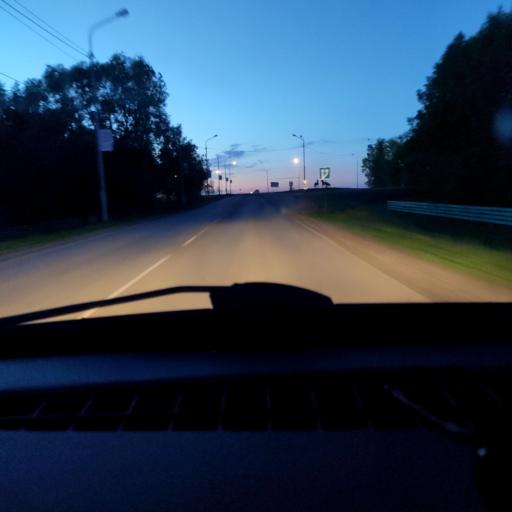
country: RU
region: Bashkortostan
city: Karmaskaly
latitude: 54.3831
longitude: 56.1787
